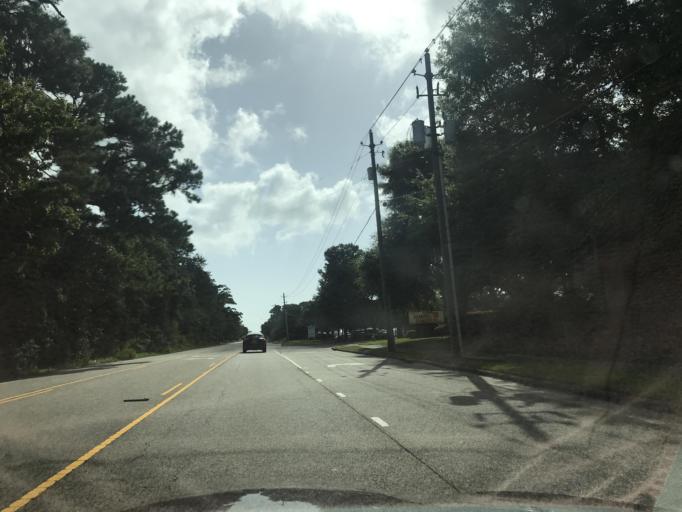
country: US
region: North Carolina
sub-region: New Hanover County
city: Seagate
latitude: 34.2205
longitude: -77.8285
